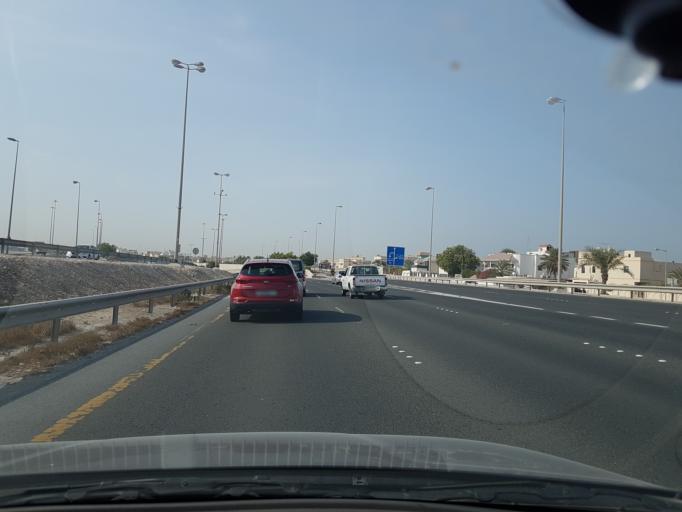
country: BH
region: Central Governorate
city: Madinat Hamad
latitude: 26.1253
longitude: 50.5061
